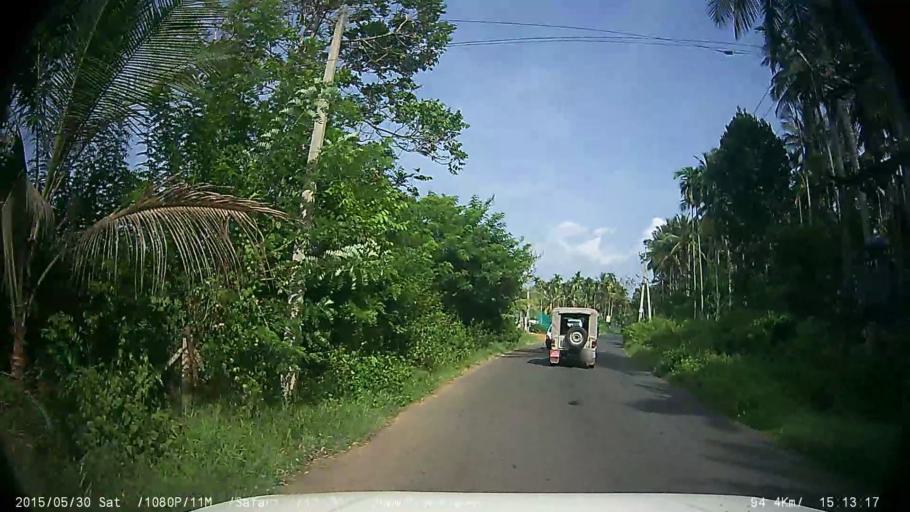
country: IN
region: Kerala
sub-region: Wayanad
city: Panamaram
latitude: 11.7919
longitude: 76.0421
